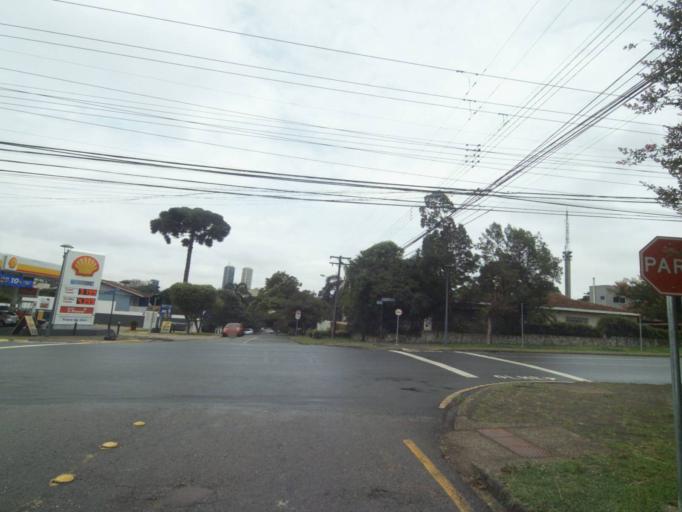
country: BR
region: Parana
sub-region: Curitiba
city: Curitiba
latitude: -25.4151
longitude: -49.2846
